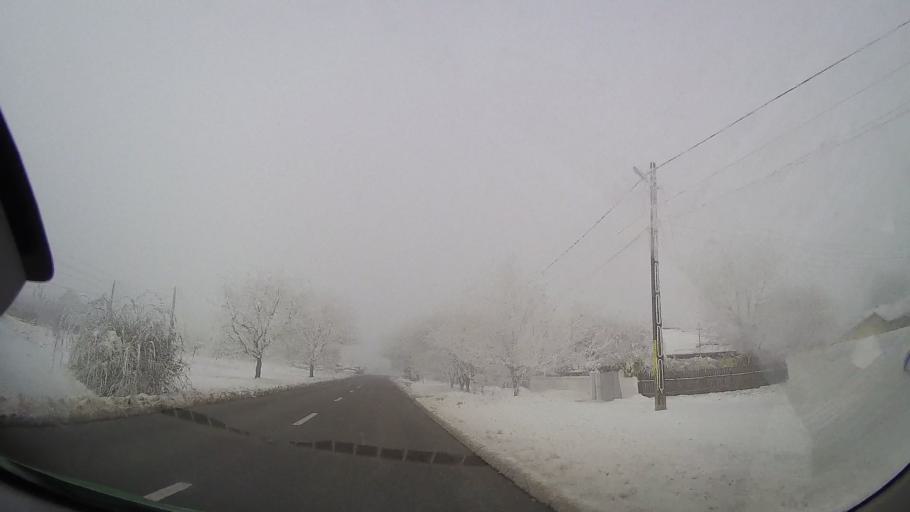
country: RO
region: Iasi
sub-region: Comuna Mircesti
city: Mircesti
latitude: 47.0894
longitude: 26.8235
